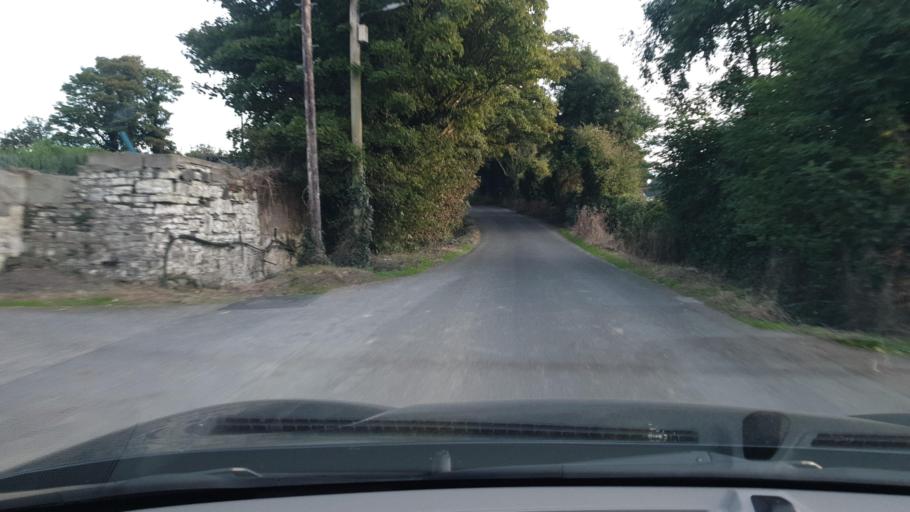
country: IE
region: Leinster
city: Balrothery
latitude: 53.5692
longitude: -6.1999
